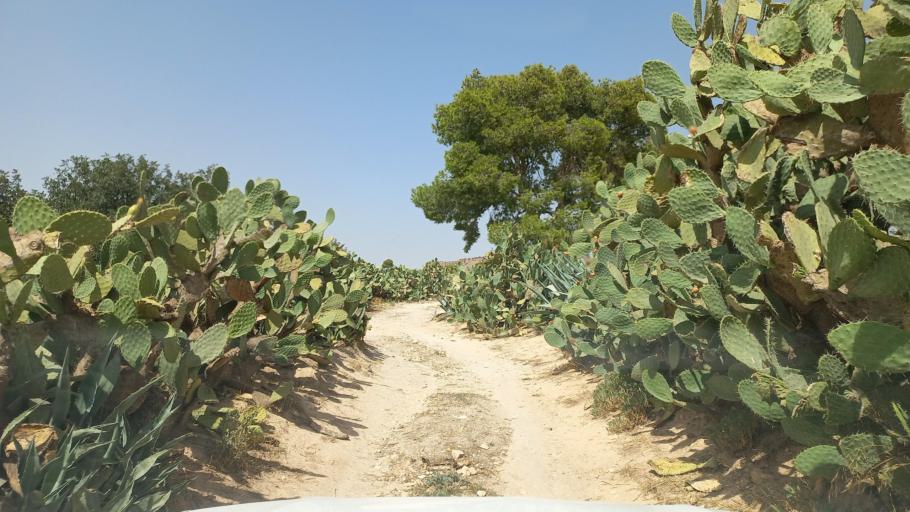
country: TN
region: Al Qasrayn
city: Sbiba
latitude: 35.4042
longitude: 8.9740
